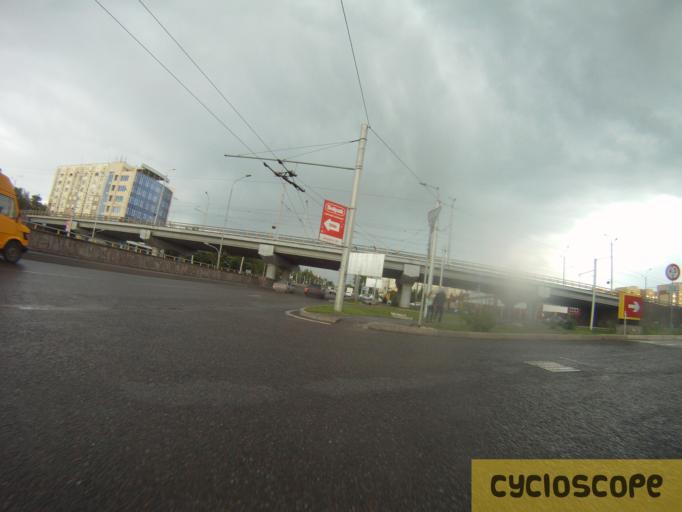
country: KZ
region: Almaty Qalasy
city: Almaty
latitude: 43.2327
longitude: 76.8419
